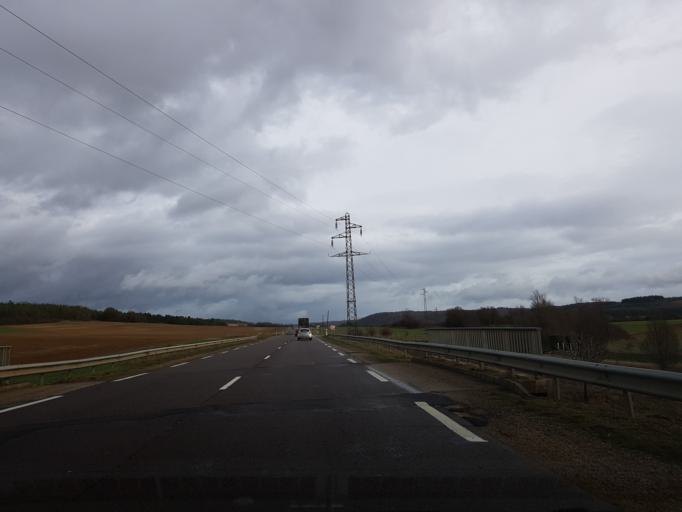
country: FR
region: Franche-Comte
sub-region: Departement de la Haute-Saone
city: Frotey-les-Vesoul
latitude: 47.6240
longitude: 6.2002
